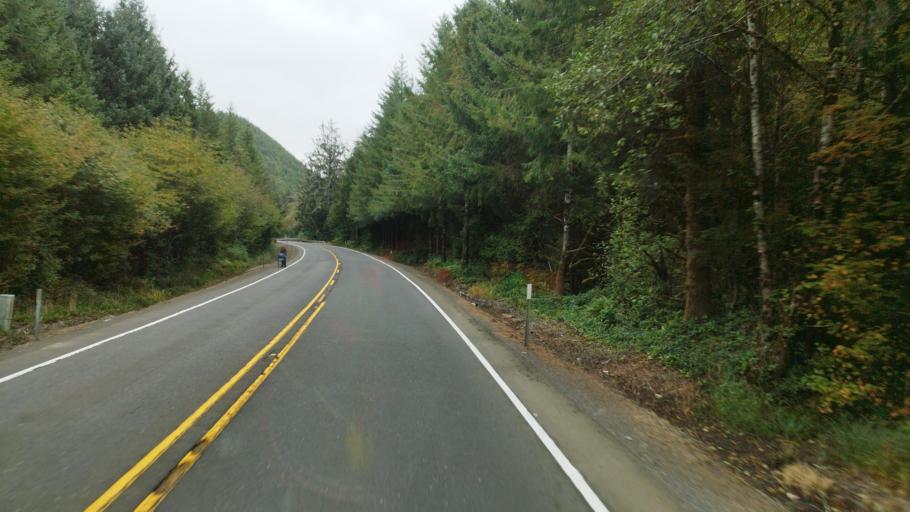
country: US
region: Oregon
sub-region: Clatsop County
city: Cannon Beach
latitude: 45.9012
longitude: -123.8629
